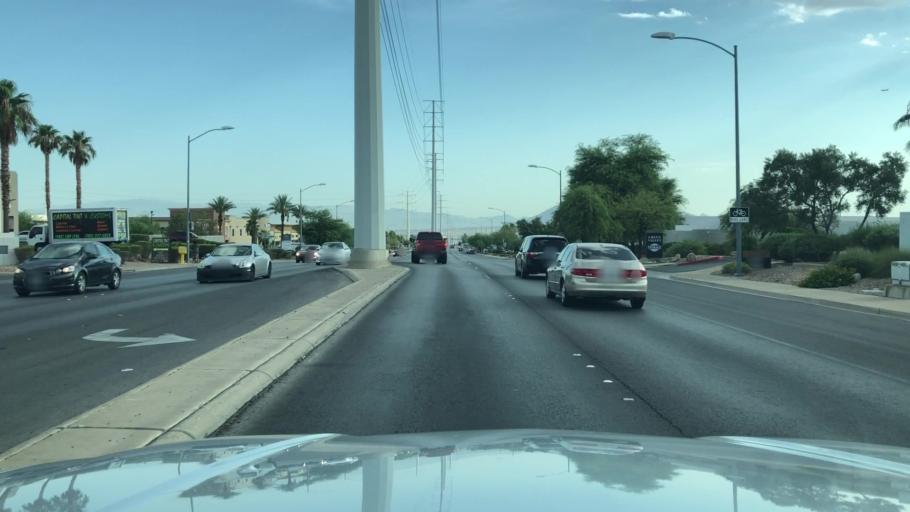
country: US
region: Nevada
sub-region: Clark County
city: Henderson
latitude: 36.0370
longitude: -115.0294
